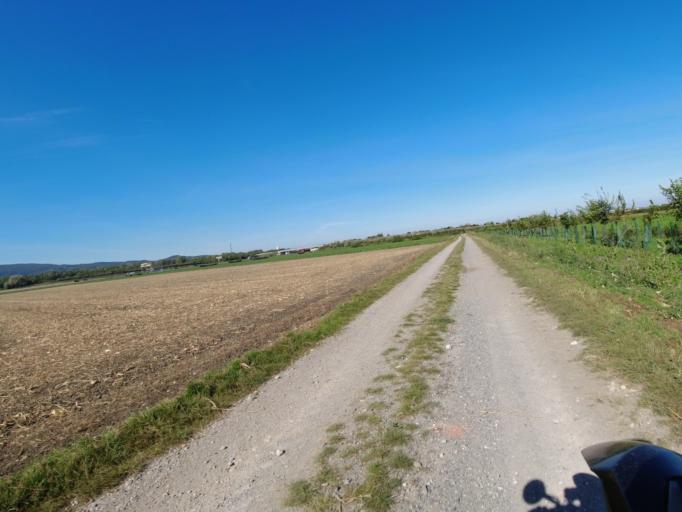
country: AT
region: Lower Austria
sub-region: Politischer Bezirk Baden
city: Trumau
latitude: 48.0251
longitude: 16.3389
